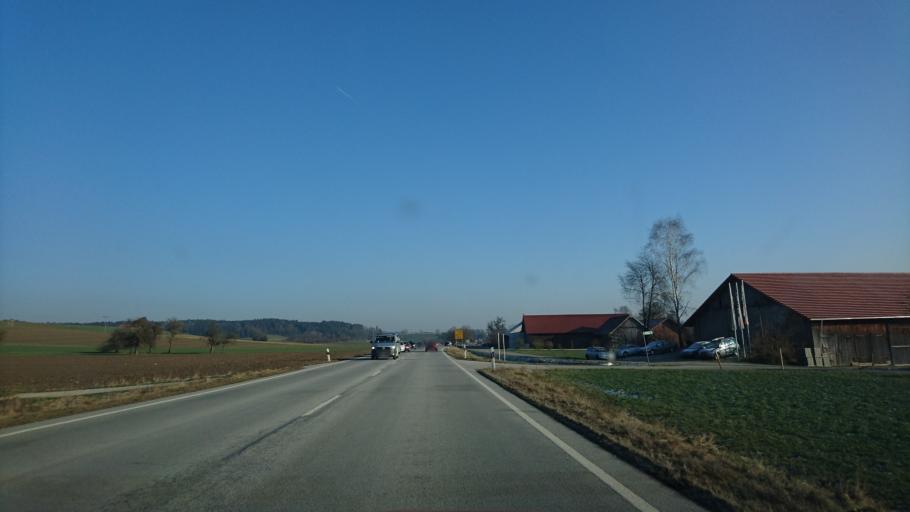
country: DE
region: Bavaria
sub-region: Lower Bavaria
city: Bad Birnbach
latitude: 48.4471
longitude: 13.0492
